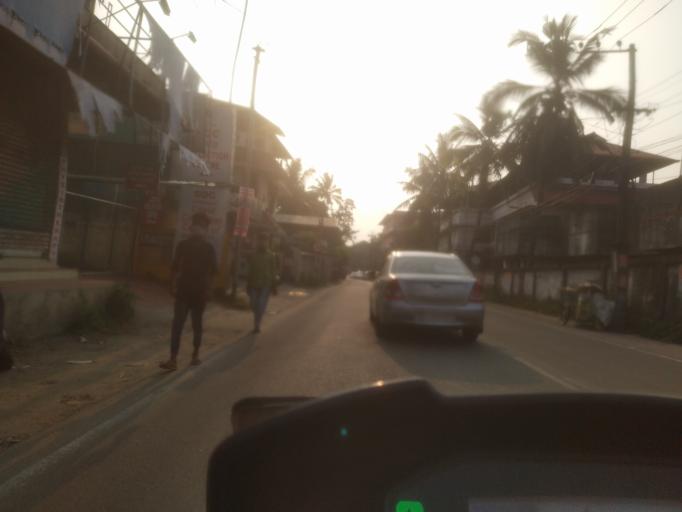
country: IN
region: Kerala
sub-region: Alappuzha
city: Arukutti
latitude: 9.9422
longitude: 76.3464
